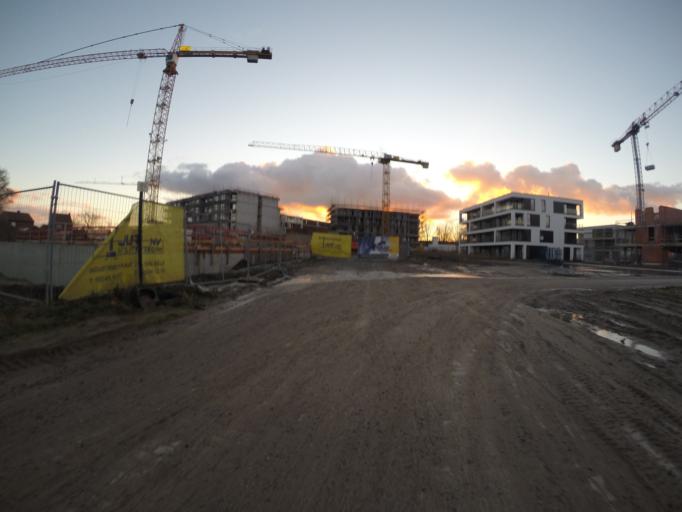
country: BE
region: Flanders
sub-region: Provincie Oost-Vlaanderen
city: Aalter
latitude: 51.0941
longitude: 3.4506
